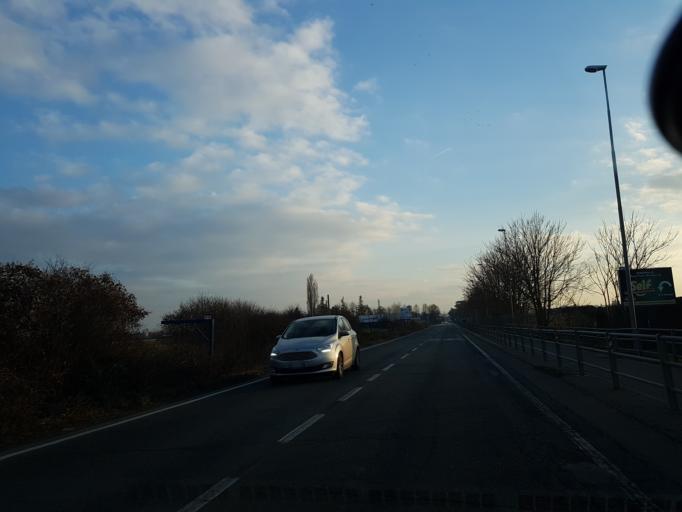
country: IT
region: Piedmont
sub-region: Provincia di Alessandria
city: Pozzolo Formigaro
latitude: 44.7836
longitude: 8.7889
